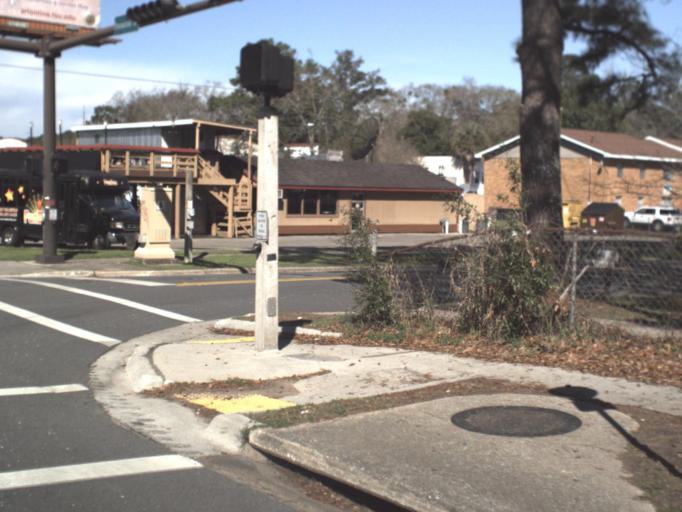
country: US
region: Florida
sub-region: Leon County
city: Tallahassee
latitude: 30.4405
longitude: -84.3142
